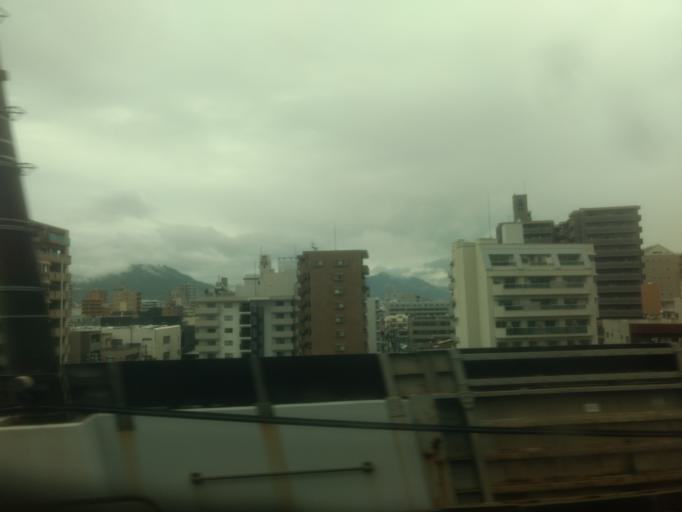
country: JP
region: Hiroshima
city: Hiroshima-shi
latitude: 34.4103
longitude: 132.4540
